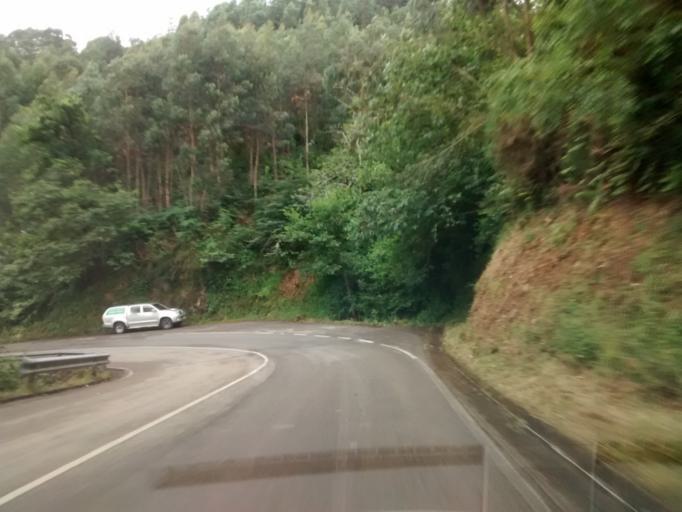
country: ES
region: Asturias
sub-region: Province of Asturias
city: Villaviciosa
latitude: 43.5321
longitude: -5.3967
